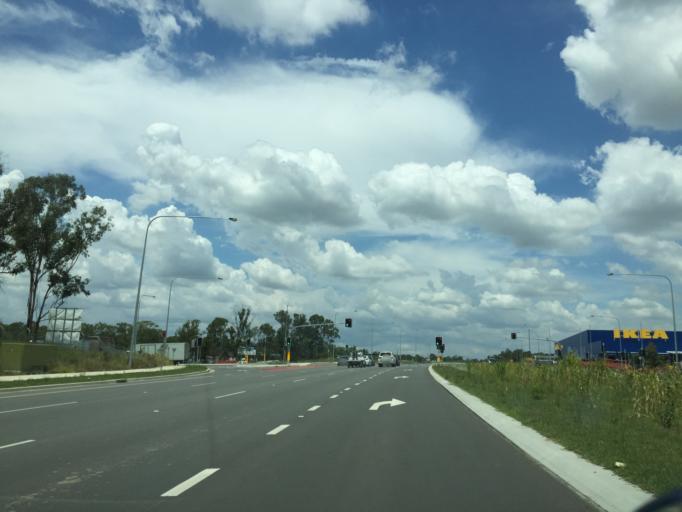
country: AU
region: New South Wales
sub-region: Blacktown
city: Hassall Grove
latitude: -33.7166
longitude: 150.8440
